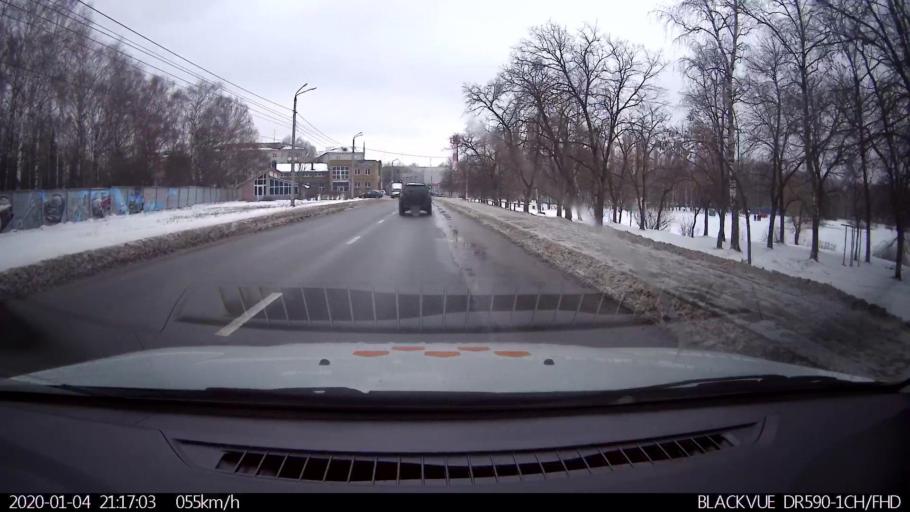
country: RU
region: Nizjnij Novgorod
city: Gorbatovka
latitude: 56.2362
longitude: 43.8515
